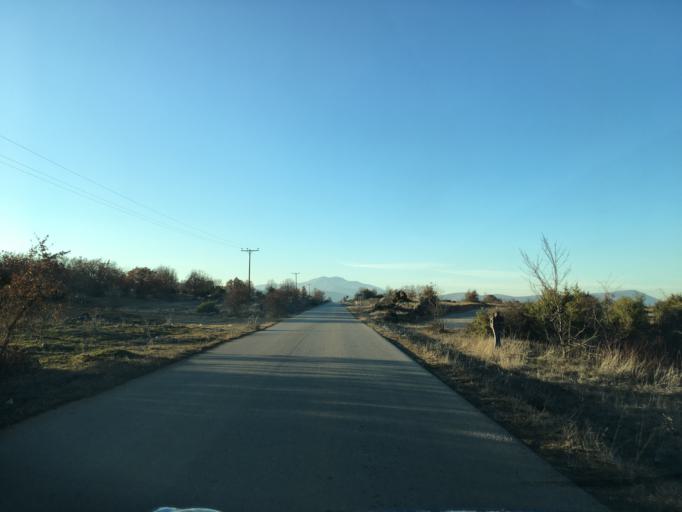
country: GR
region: West Macedonia
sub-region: Nomos Kozanis
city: Kozani
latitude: 40.2696
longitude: 21.7414
